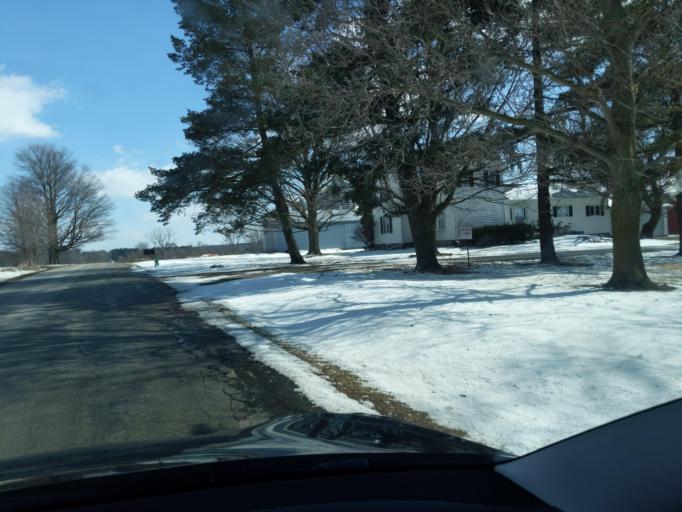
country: US
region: Michigan
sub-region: Ingham County
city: Mason
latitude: 42.6110
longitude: -84.4193
